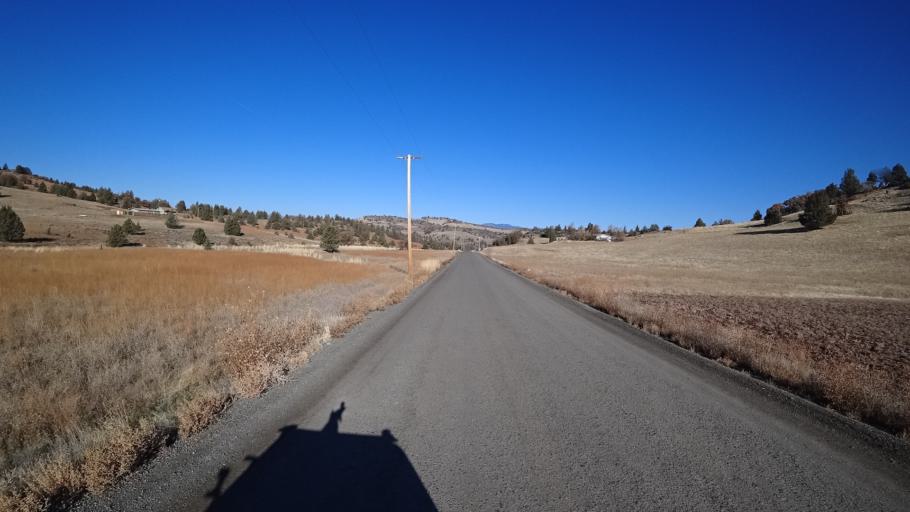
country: US
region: California
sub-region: Siskiyou County
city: Montague
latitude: 41.8815
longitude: -122.4248
